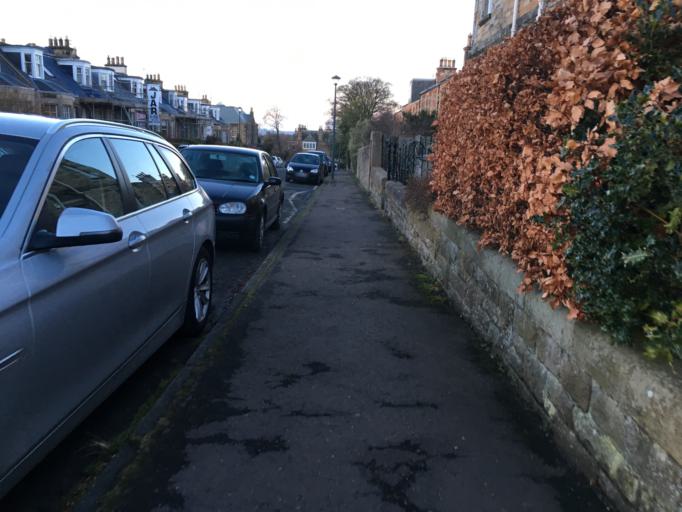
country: GB
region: Scotland
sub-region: Edinburgh
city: Edinburgh
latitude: 55.9213
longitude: -3.2173
